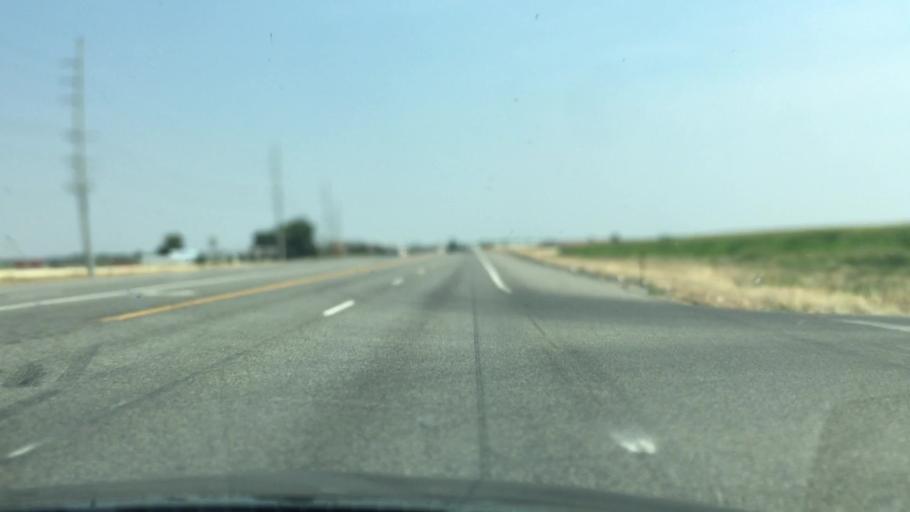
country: US
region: Idaho
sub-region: Twin Falls County
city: Twin Falls
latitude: 42.5927
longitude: -114.5159
